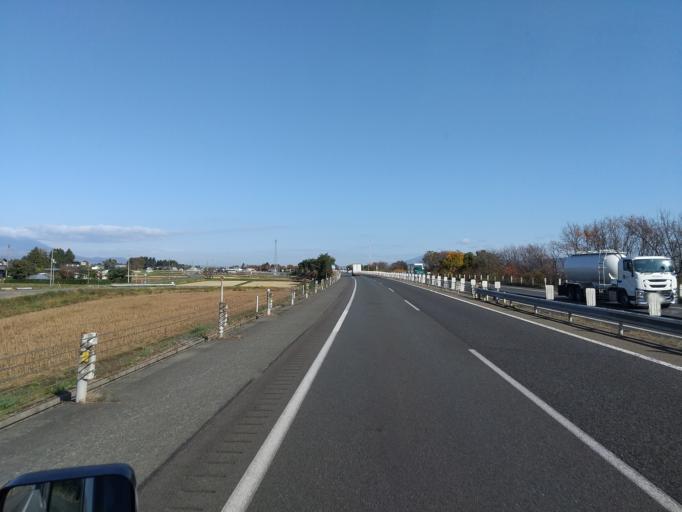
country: JP
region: Iwate
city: Morioka-shi
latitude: 39.6124
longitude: 141.1289
